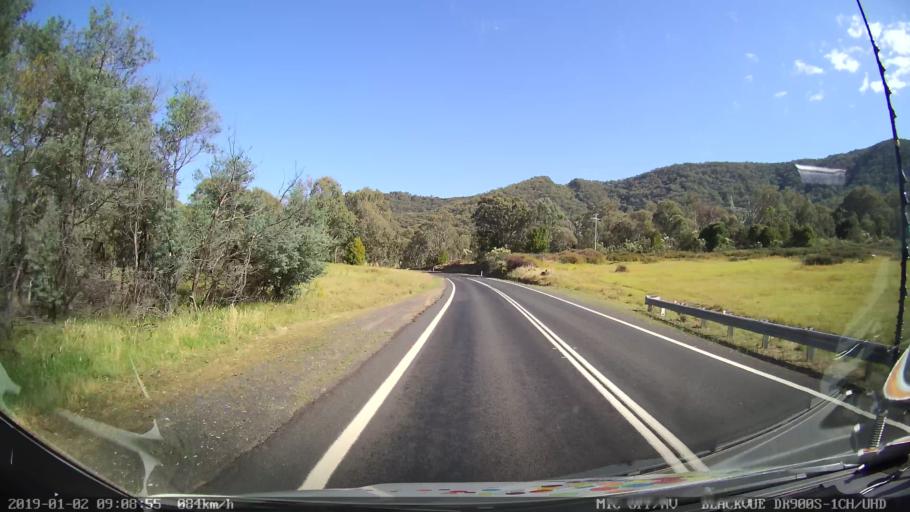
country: AU
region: New South Wales
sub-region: Tumut Shire
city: Tumut
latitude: -35.5276
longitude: 148.2862
